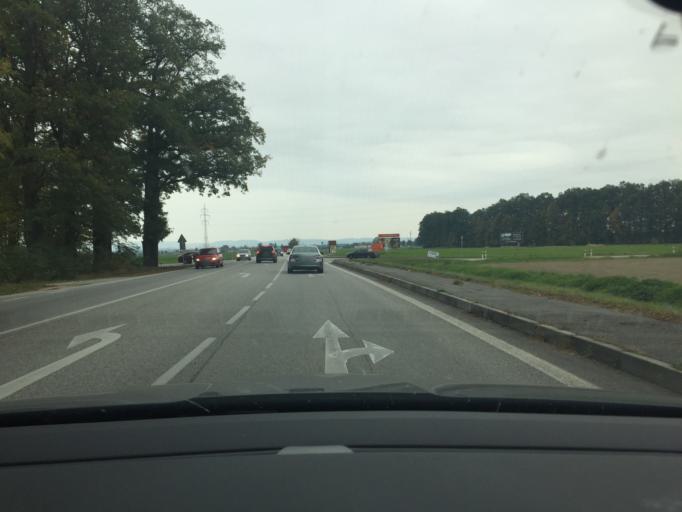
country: CZ
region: Jihocesky
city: Zliv
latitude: 49.0244
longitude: 14.3890
